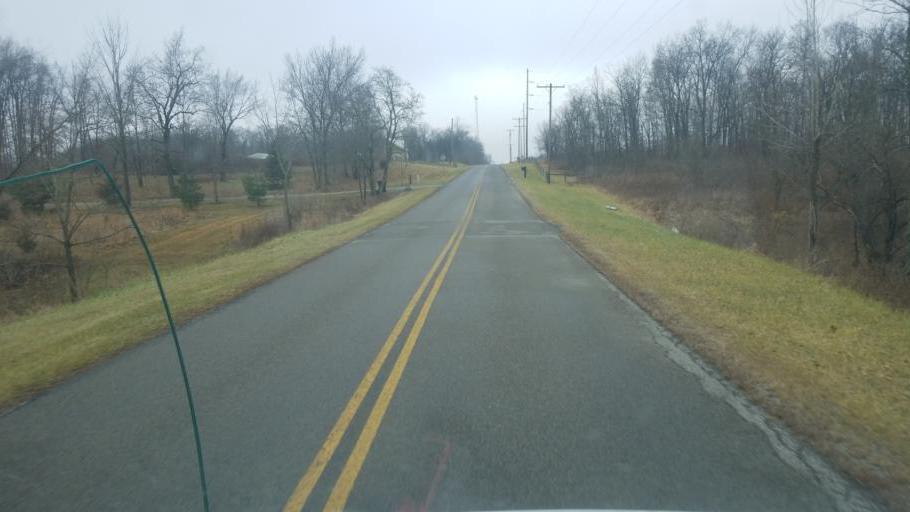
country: US
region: Ohio
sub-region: Champaign County
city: North Lewisburg
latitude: 40.3124
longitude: -83.5851
